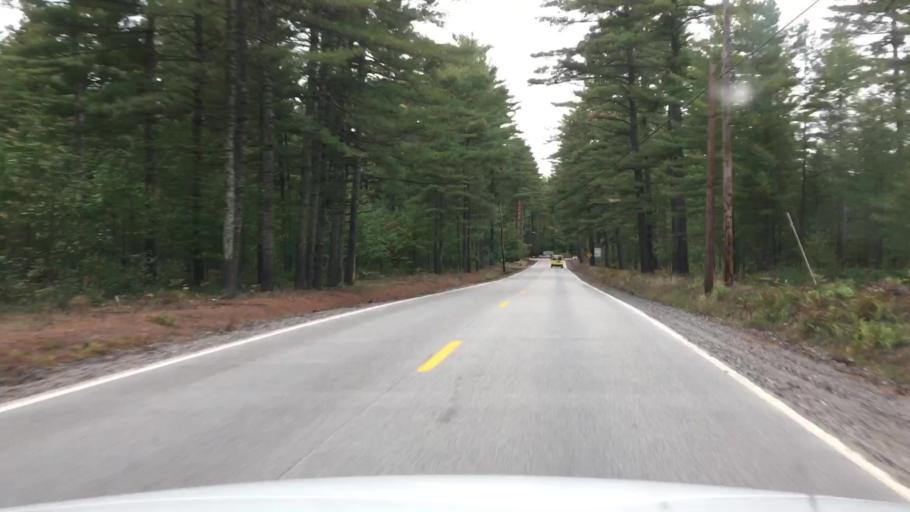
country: US
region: Maine
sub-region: Cumberland County
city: Harrison
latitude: 44.2276
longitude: -70.7023
